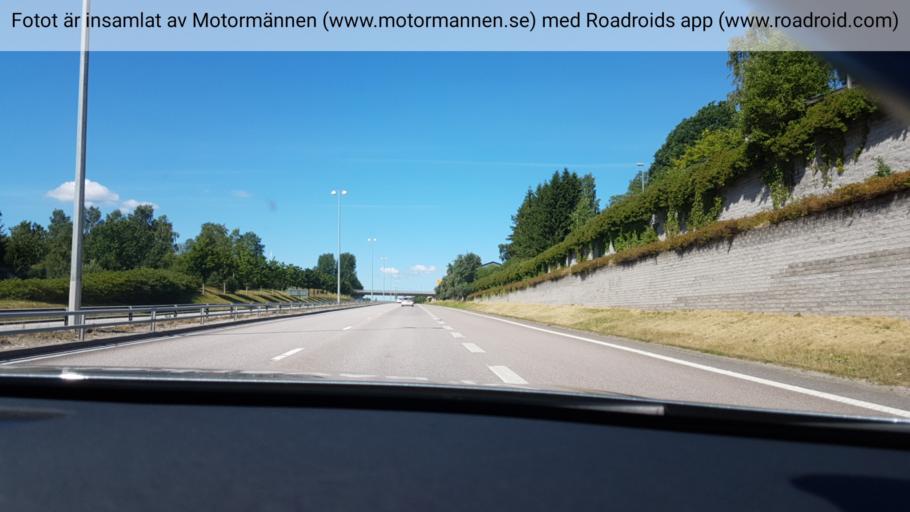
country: SE
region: Vaestra Goetaland
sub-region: Boras Kommun
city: Ganghester
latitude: 57.7281
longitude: 13.0149
